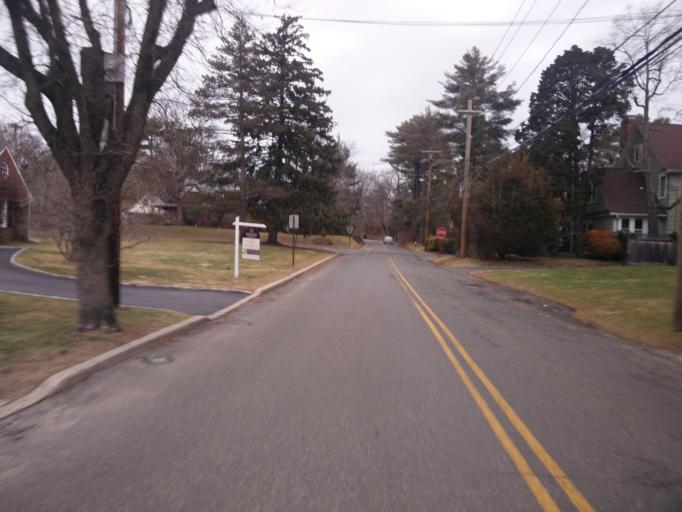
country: US
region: New York
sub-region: Nassau County
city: Glen Cove
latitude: 40.8714
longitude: -73.6401
